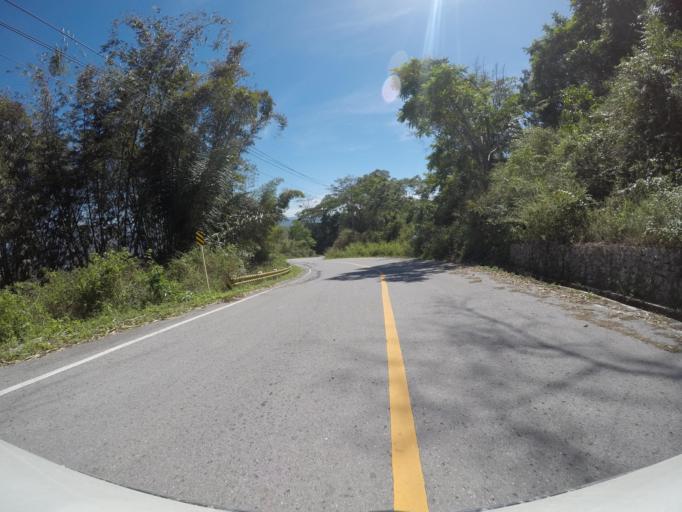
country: TL
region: Manufahi
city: Same
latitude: -8.8990
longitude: 125.9800
